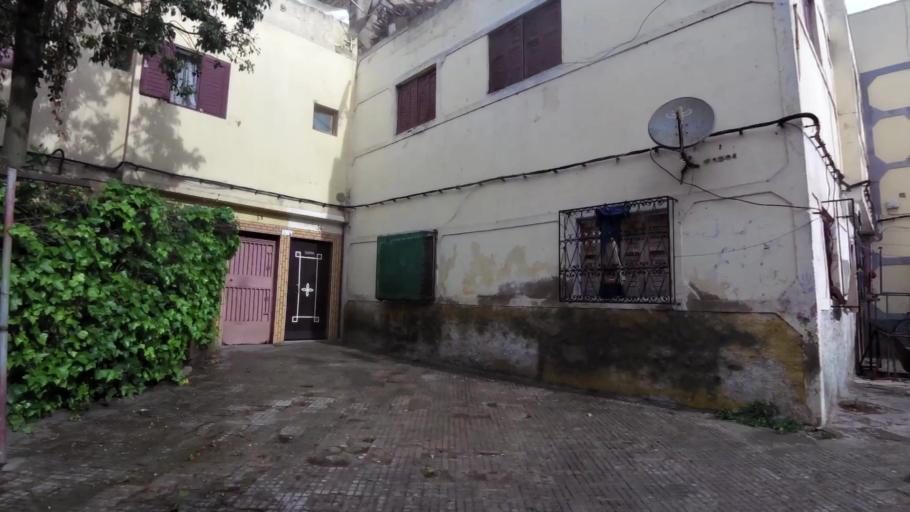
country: MA
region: Grand Casablanca
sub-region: Casablanca
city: Casablanca
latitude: 33.5585
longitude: -7.6859
